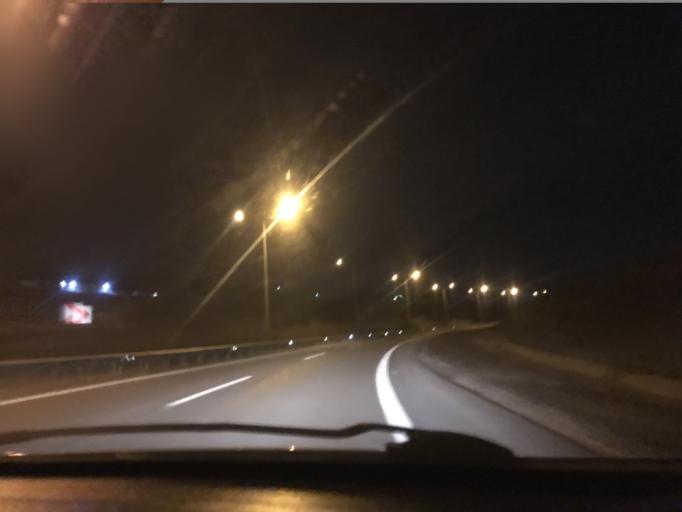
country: TR
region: Ankara
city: Etimesgut
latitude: 39.8634
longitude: 32.6261
